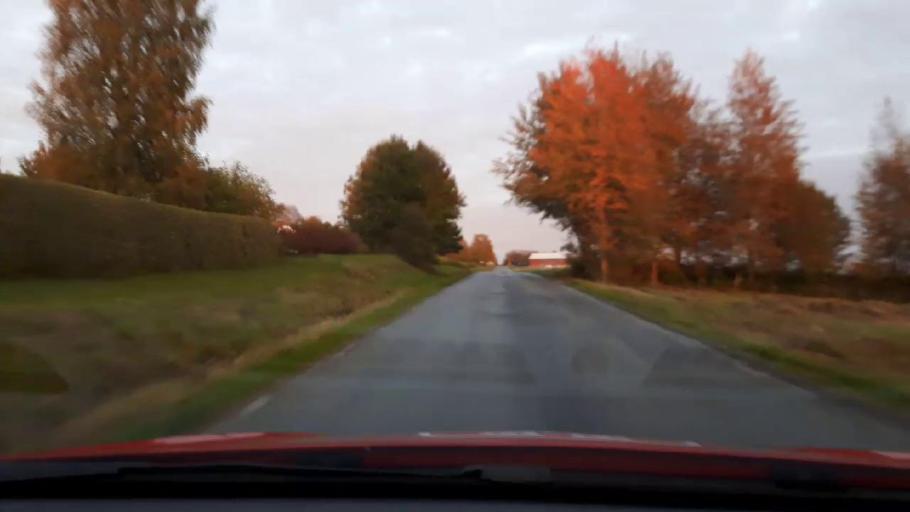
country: SE
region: Jaemtland
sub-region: OEstersunds Kommun
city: Ostersund
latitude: 63.2429
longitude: 14.5476
